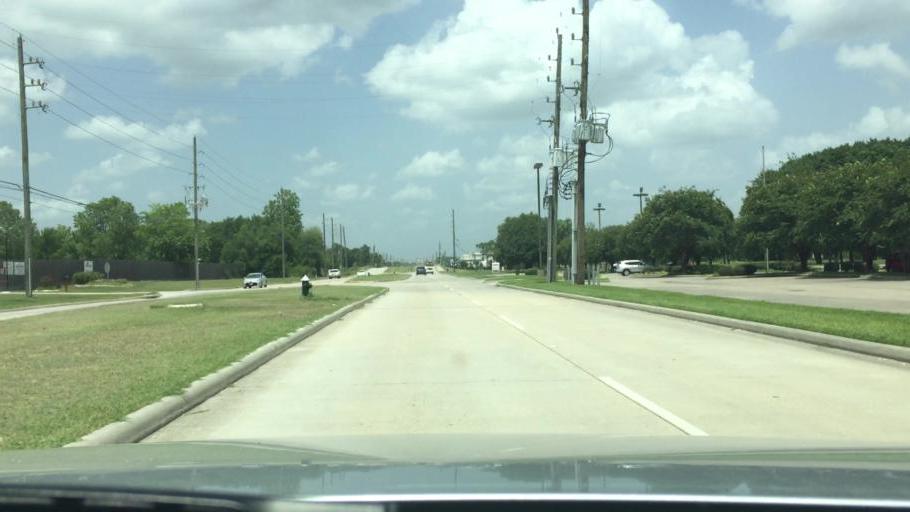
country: US
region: Texas
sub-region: Harris County
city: Hudson
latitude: 29.9463
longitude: -95.5176
